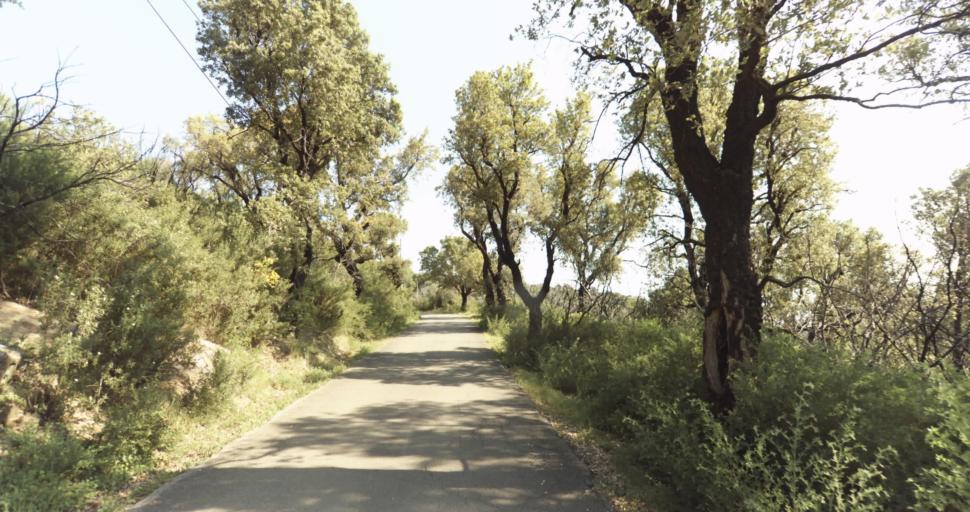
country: FR
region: Corsica
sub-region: Departement de la Haute-Corse
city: Biguglia
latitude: 42.6355
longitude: 9.4168
